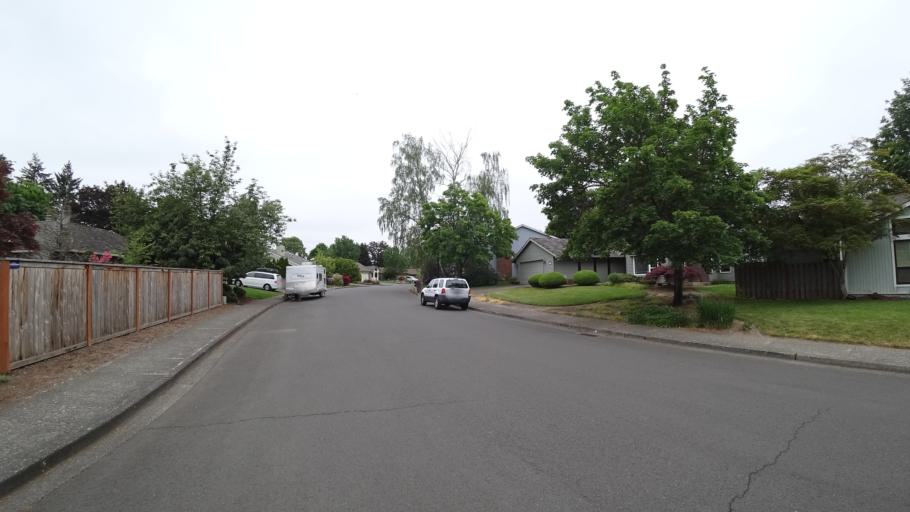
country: US
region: Oregon
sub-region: Washington County
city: Rockcreek
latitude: 45.5611
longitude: -122.8904
